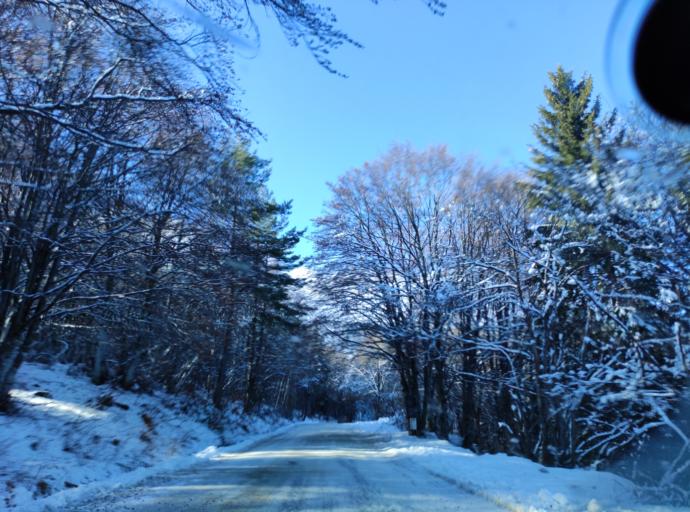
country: BG
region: Sofia-Capital
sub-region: Stolichna Obshtina
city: Sofia
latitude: 42.6044
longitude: 23.3031
